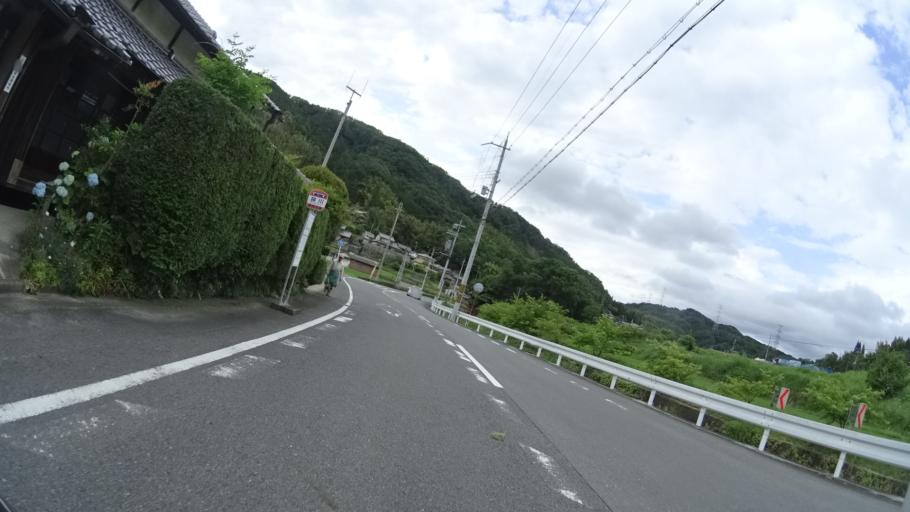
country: JP
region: Nara
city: Nara-shi
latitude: 34.7385
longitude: 135.9146
